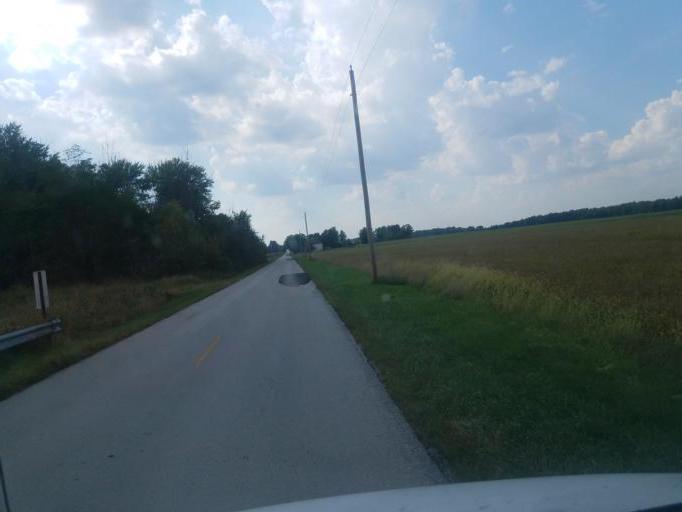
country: US
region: Ohio
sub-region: Hardin County
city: Kenton
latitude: 40.7458
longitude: -83.6056
